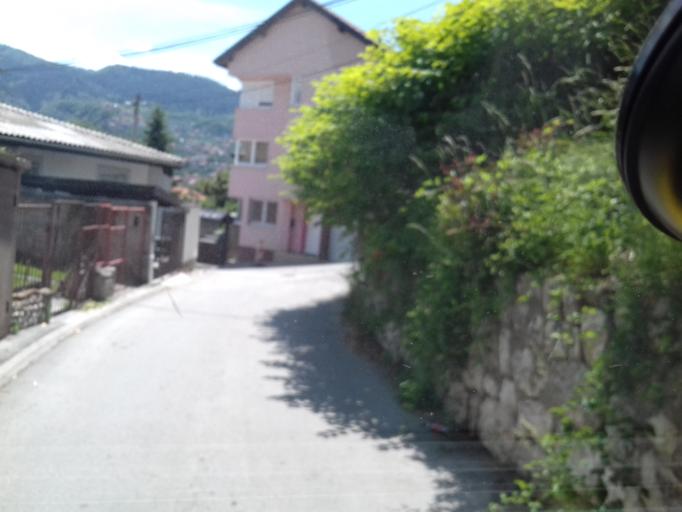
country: BA
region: Federation of Bosnia and Herzegovina
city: Kobilja Glava
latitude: 43.8644
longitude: 18.4243
